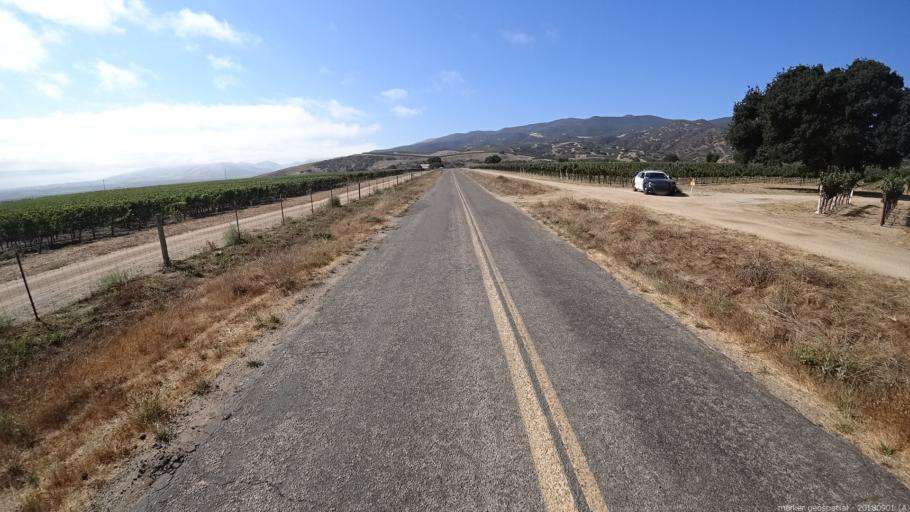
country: US
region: California
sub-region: Monterey County
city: Soledad
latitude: 36.3429
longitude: -121.3420
